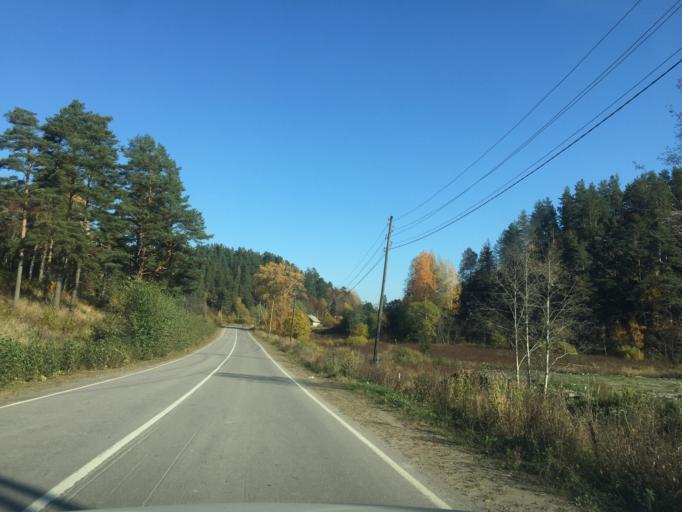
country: RU
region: Leningrad
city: Kuznechnoye
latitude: 61.2999
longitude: 29.9097
